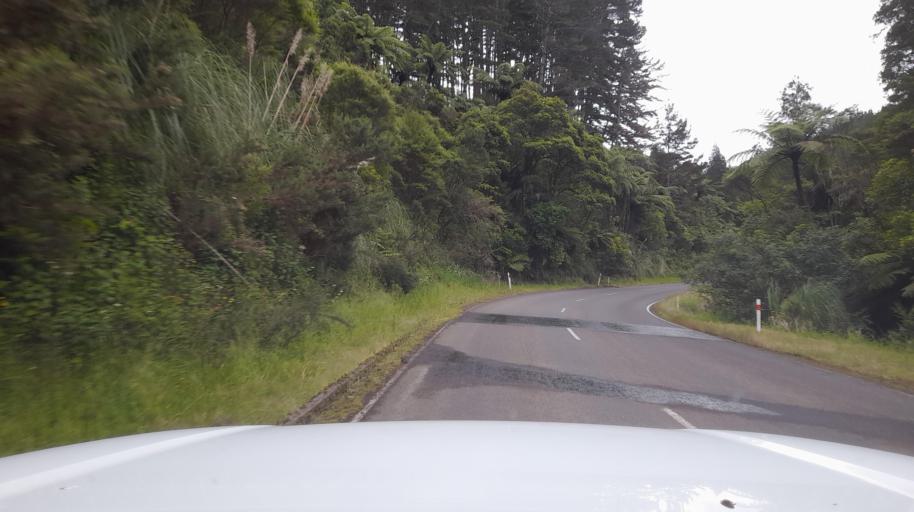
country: NZ
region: Northland
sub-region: Far North District
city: Kaitaia
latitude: -35.3643
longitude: 173.3935
